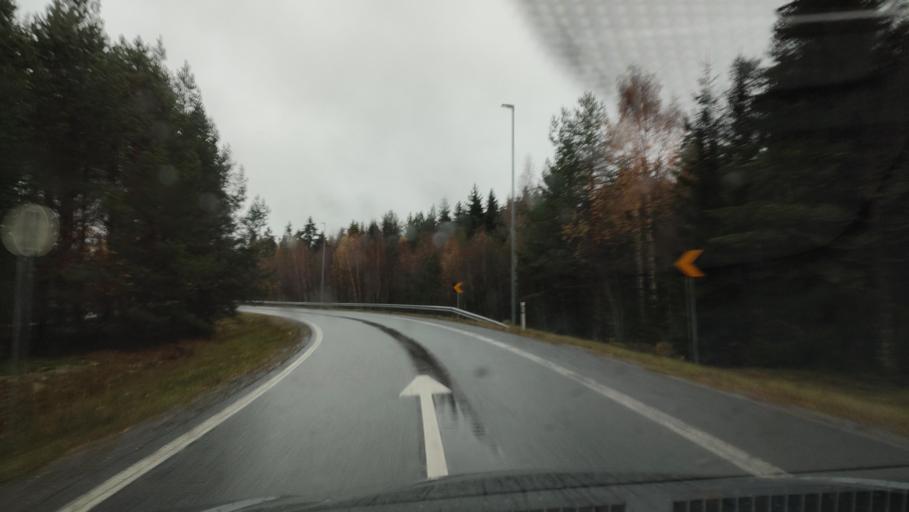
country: FI
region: Ostrobothnia
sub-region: Vaasa
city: Ristinummi
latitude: 63.0554
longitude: 21.7098
